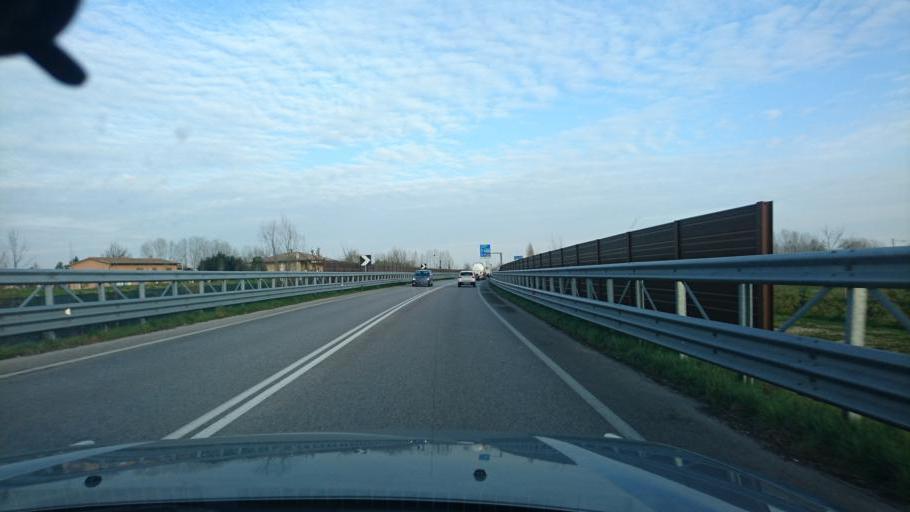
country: IT
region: Veneto
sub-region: Provincia di Padova
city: Tencarola
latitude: 45.3834
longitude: 11.8188
